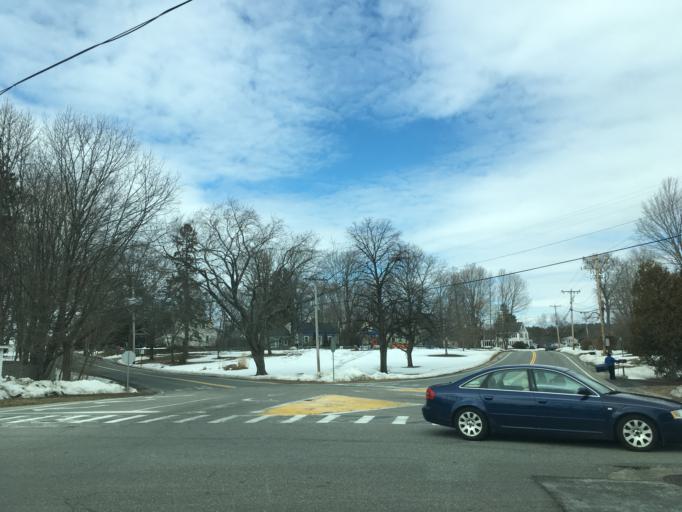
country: US
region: New Hampshire
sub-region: Rockingham County
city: Hampton
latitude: 42.9383
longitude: -70.8187
